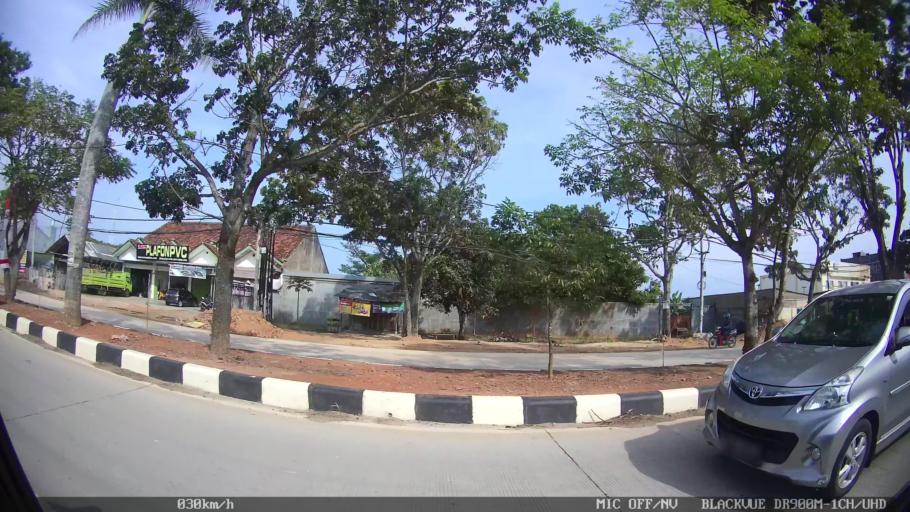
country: ID
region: Lampung
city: Kedaton
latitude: -5.3731
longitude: 105.2967
